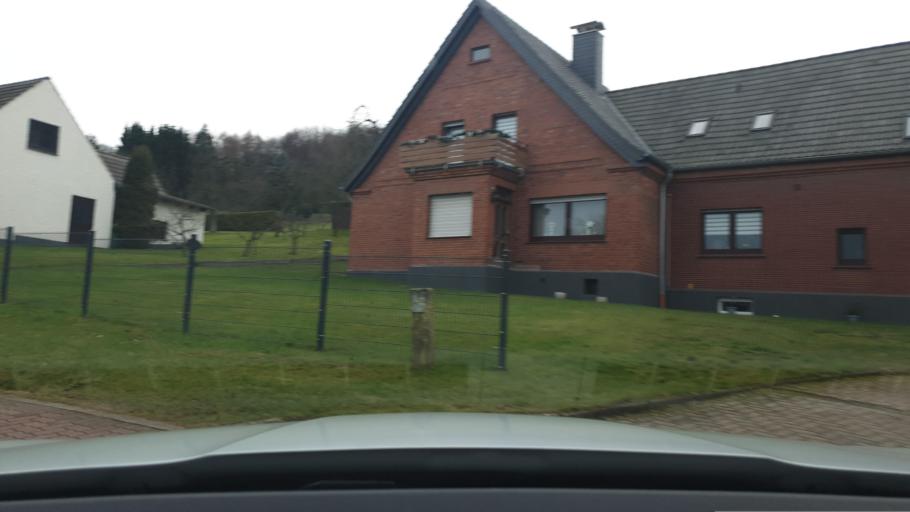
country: DE
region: North Rhine-Westphalia
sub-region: Regierungsbezirk Detmold
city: Hille
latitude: 52.2863
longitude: 8.7390
